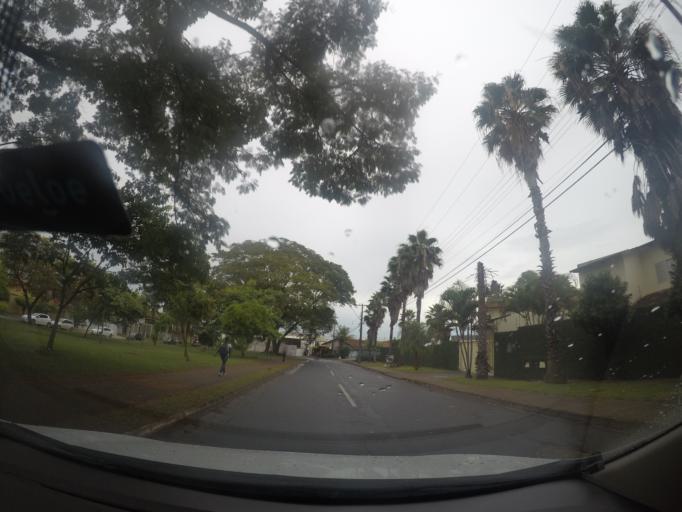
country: BR
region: Goias
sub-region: Goiania
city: Goiania
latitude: -16.6375
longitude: -49.2352
